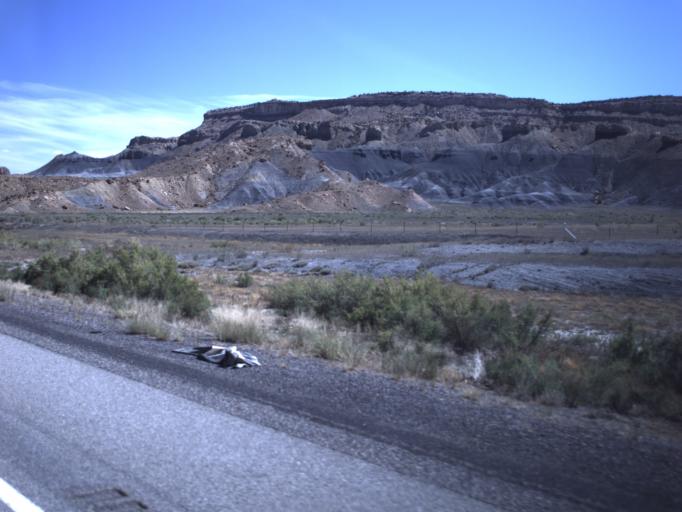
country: US
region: Utah
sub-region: Emery County
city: Ferron
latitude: 38.8097
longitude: -111.2400
